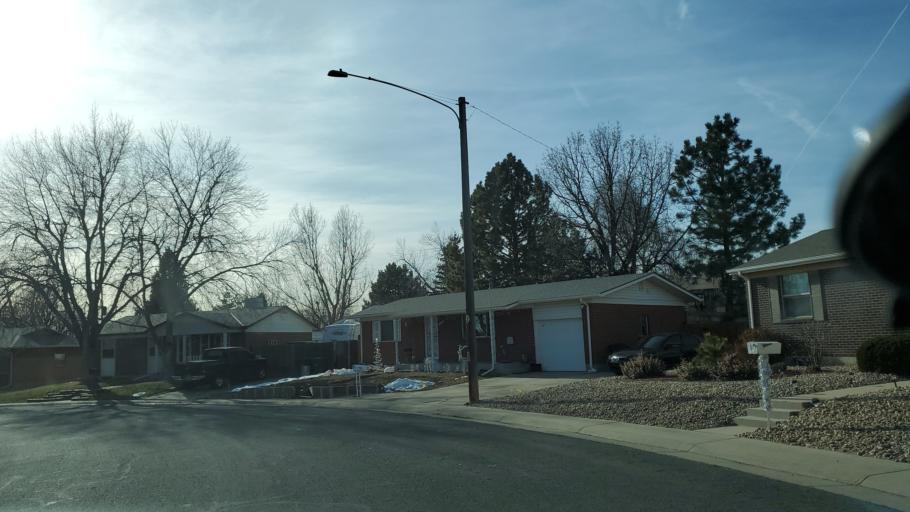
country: US
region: Colorado
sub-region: Adams County
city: Northglenn
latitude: 39.9112
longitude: -104.9641
